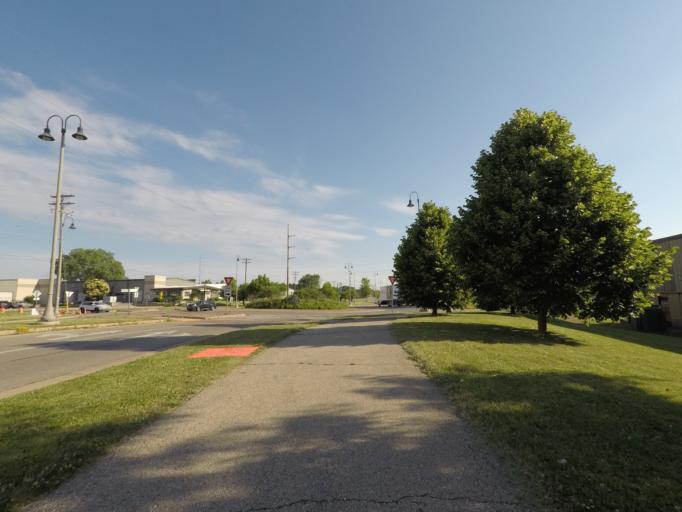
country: US
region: Wisconsin
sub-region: Dane County
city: Monona
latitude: 43.0404
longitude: -89.3544
